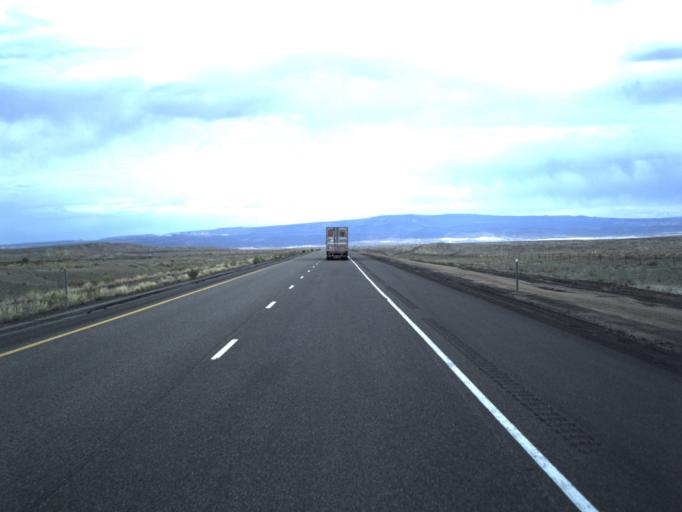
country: US
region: Utah
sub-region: Grand County
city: Moab
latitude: 38.9366
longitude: -109.4811
